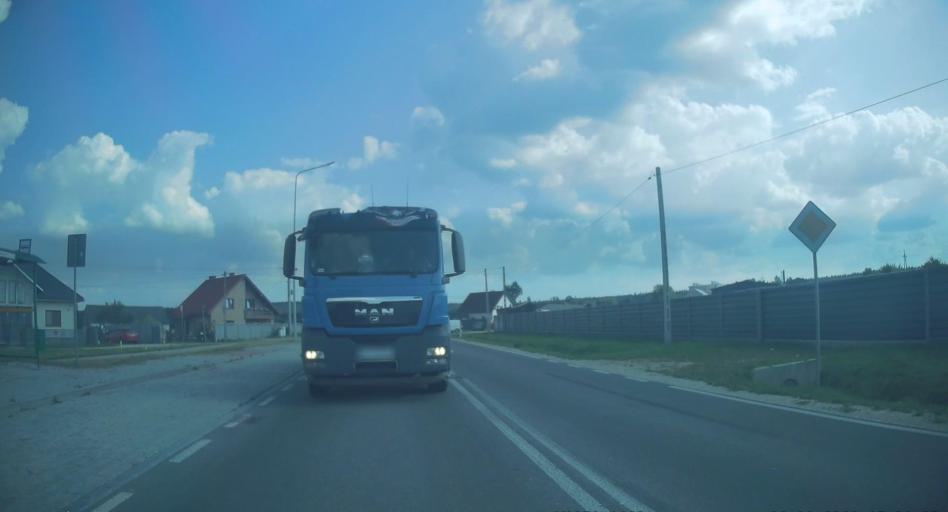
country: PL
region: Swietokrzyskie
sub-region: Powiat konecki
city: Radoszyce
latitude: 51.0350
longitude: 20.2860
